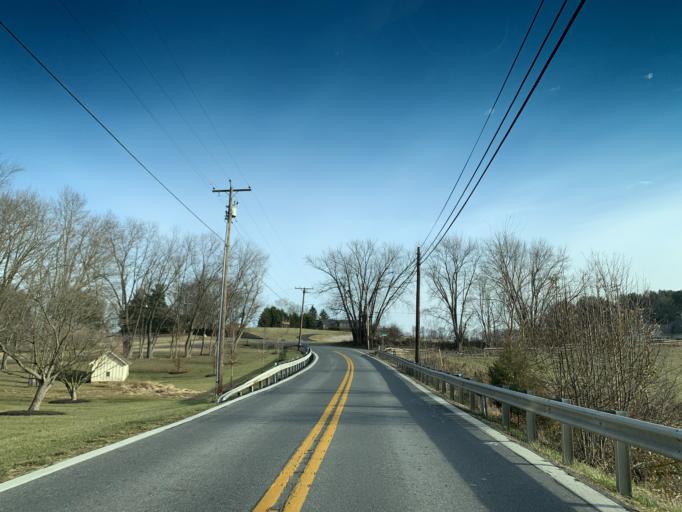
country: US
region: Maryland
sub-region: Carroll County
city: Hampstead
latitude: 39.6037
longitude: -76.7944
